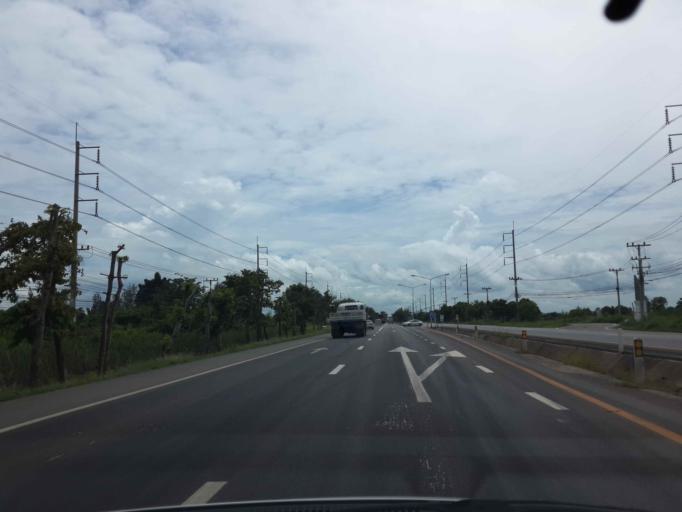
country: TH
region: Ratchaburi
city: Pak Tho
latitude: 13.4211
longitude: 99.8090
